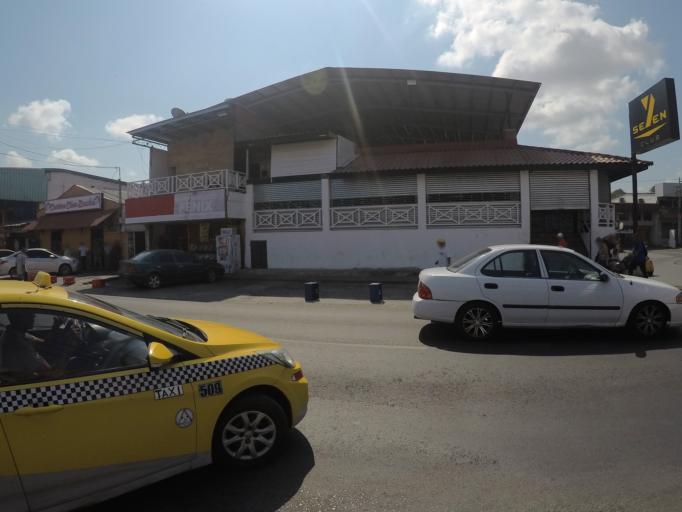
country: PA
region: Panama
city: La Chorrera
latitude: 8.8856
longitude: -79.7928
